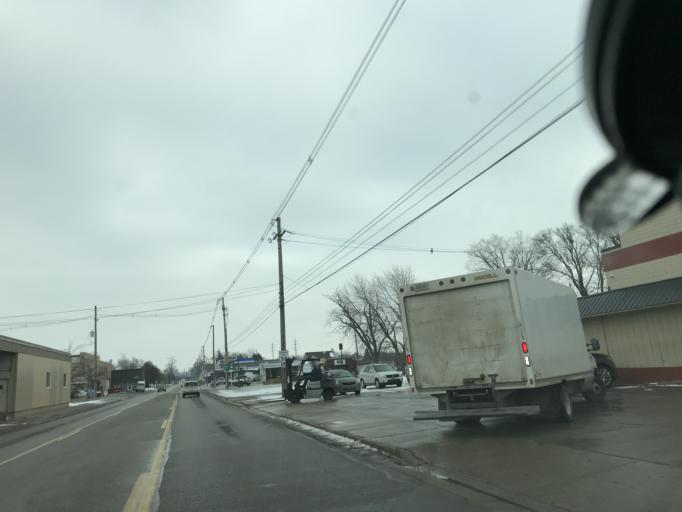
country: US
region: Michigan
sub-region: Ottawa County
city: Zeeland
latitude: 42.8138
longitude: -86.0177
